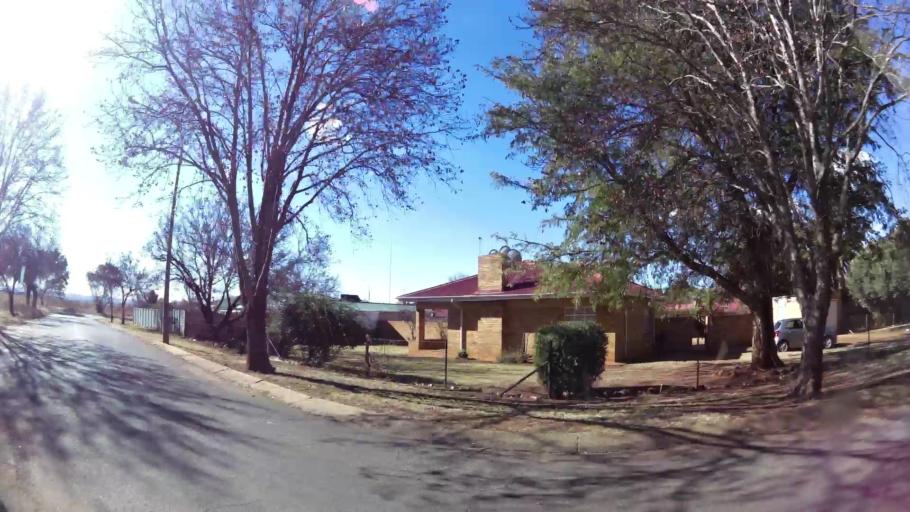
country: ZA
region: Gauteng
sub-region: West Rand District Municipality
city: Carletonville
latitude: -26.3609
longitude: 27.3652
